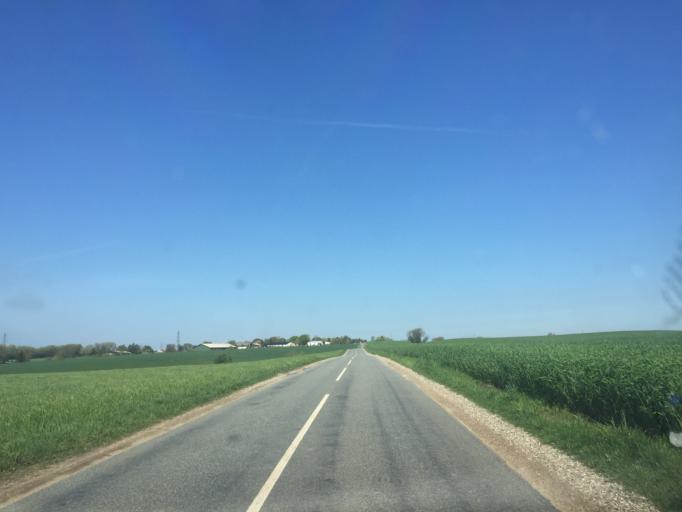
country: DK
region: Capital Region
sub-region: Egedal Kommune
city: Vekso
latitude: 55.7190
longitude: 12.2437
